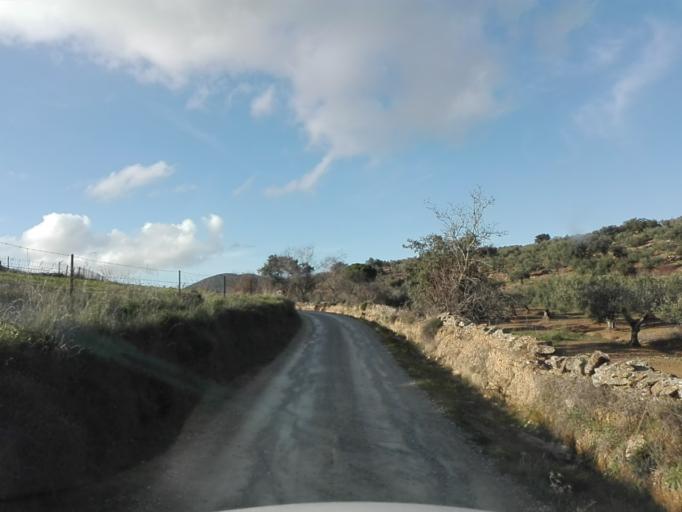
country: ES
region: Extremadura
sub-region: Provincia de Badajoz
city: Trasierra
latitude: 38.1827
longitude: -5.9827
